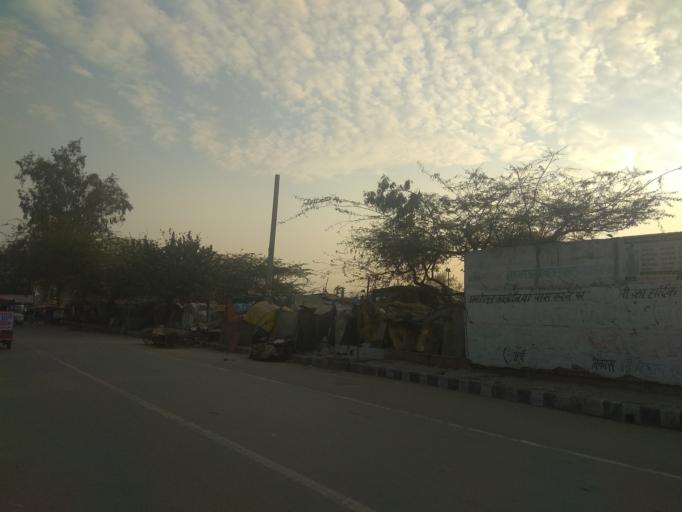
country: IN
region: NCT
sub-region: West Delhi
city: Nangloi Jat
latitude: 28.6356
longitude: 77.0622
